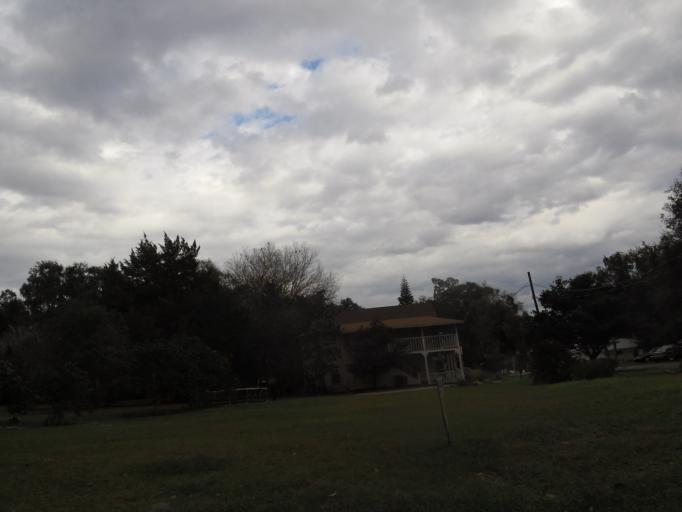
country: US
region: Florida
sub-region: Putnam County
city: Crescent City
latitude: 29.4330
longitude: -81.5081
